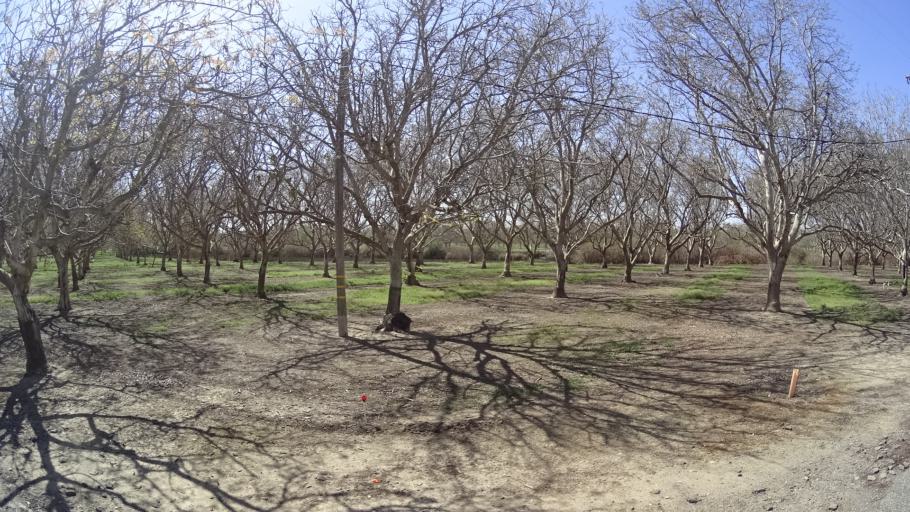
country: US
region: California
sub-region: Glenn County
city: Willows
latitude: 39.4810
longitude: -122.0231
